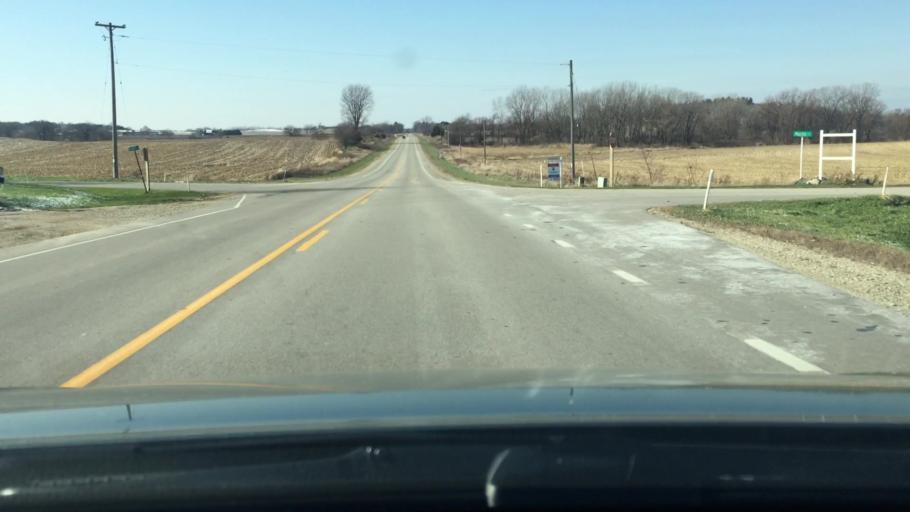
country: US
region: Wisconsin
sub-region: Jefferson County
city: Lake Mills
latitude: 43.0077
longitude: -88.9039
